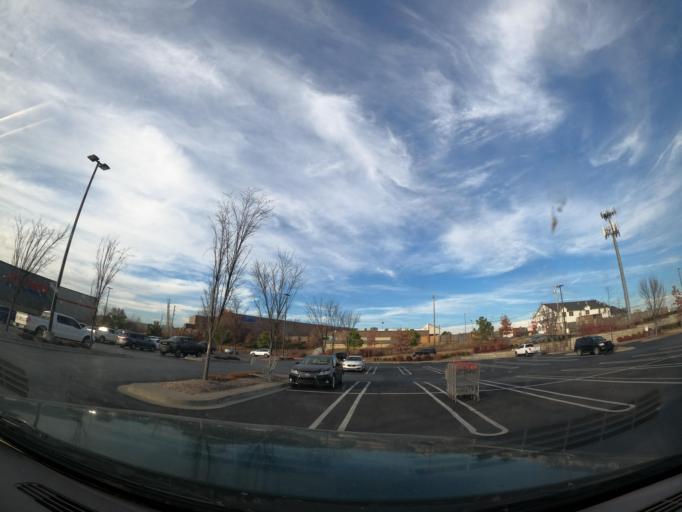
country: US
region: Oklahoma
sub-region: Tulsa County
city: Bixby
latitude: 36.0149
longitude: -95.8880
